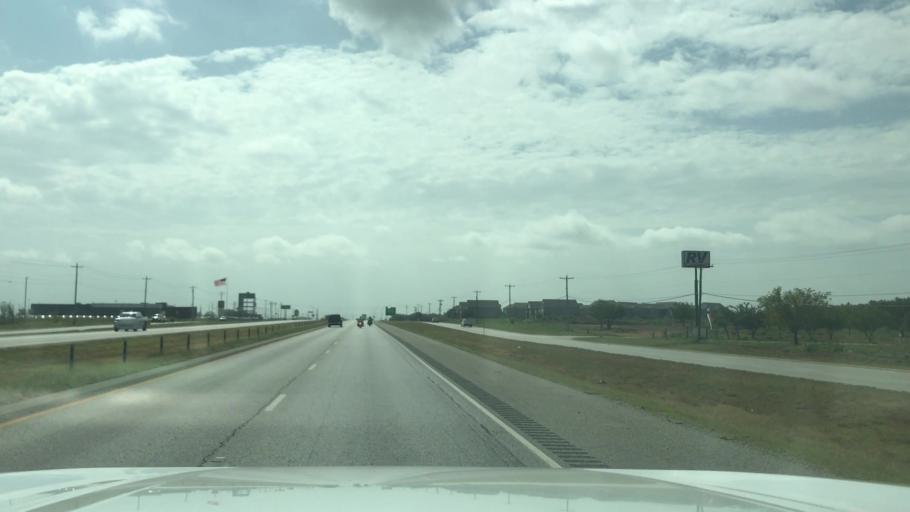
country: US
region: Texas
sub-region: Taylor County
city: Abilene
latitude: 32.4863
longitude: -99.7137
